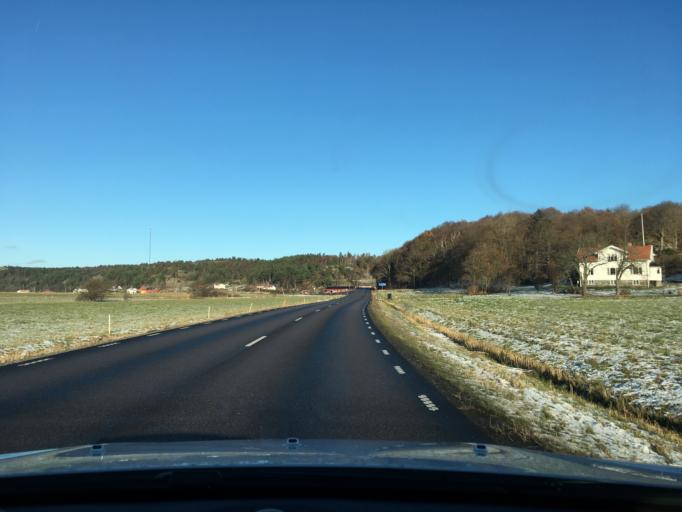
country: SE
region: Vaestra Goetaland
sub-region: Tjorns Kommun
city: Myggenas
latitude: 58.0305
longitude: 11.6570
